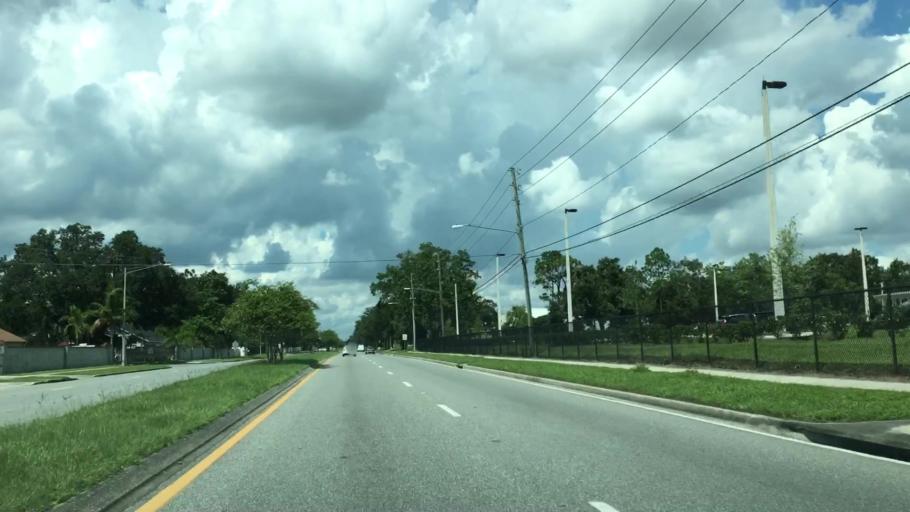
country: US
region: Florida
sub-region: Orange County
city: Conway
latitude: 28.4990
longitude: -81.2974
